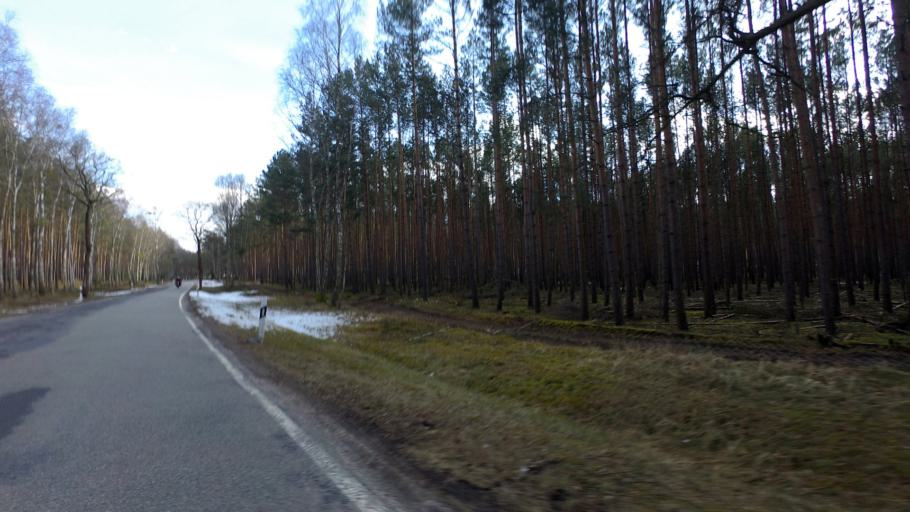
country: DE
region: Brandenburg
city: Marienwerder
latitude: 52.7989
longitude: 13.5949
